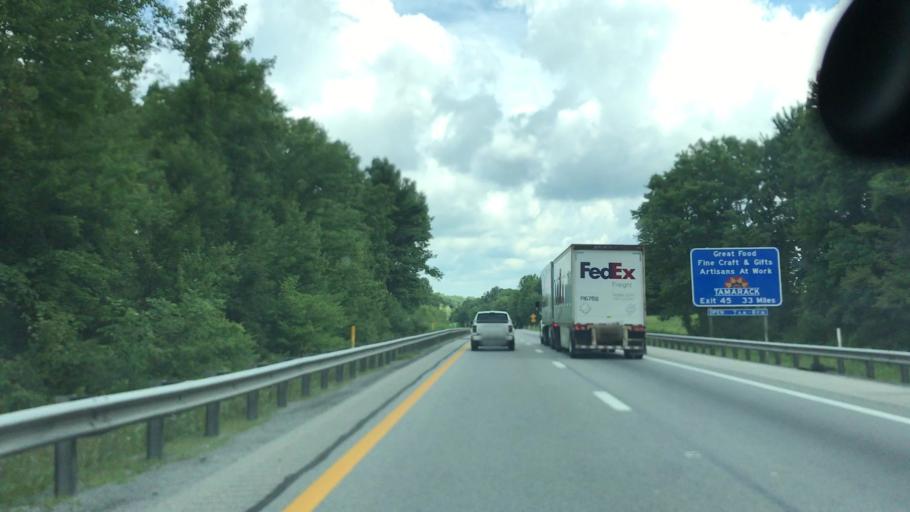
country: US
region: West Virginia
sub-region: Mercer County
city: Athens
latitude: 37.4021
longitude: -81.0616
